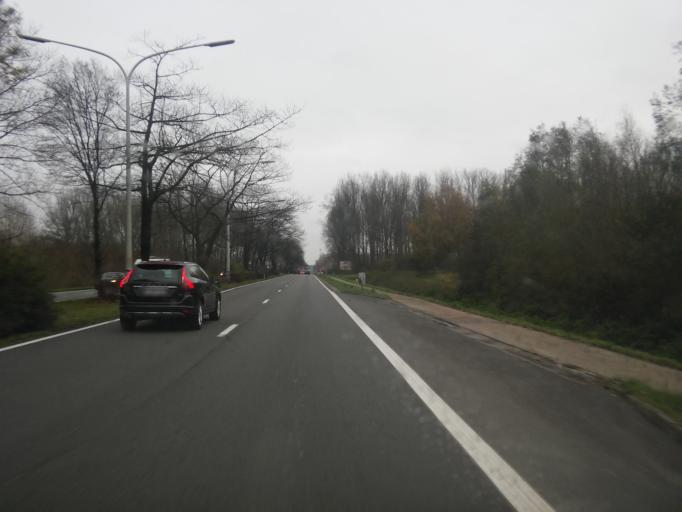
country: BE
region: Flanders
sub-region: Provincie Antwerpen
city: Puurs
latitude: 51.0860
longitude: 4.2814
